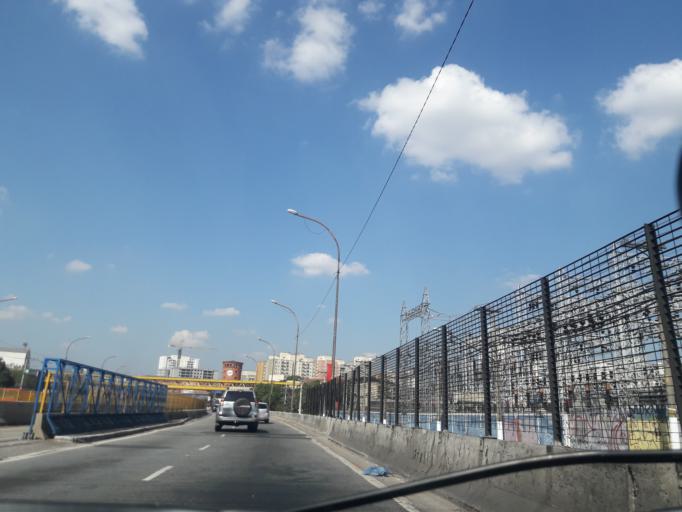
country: BR
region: Sao Paulo
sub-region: Sao Paulo
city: Sao Paulo
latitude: -23.5550
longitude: -46.6244
